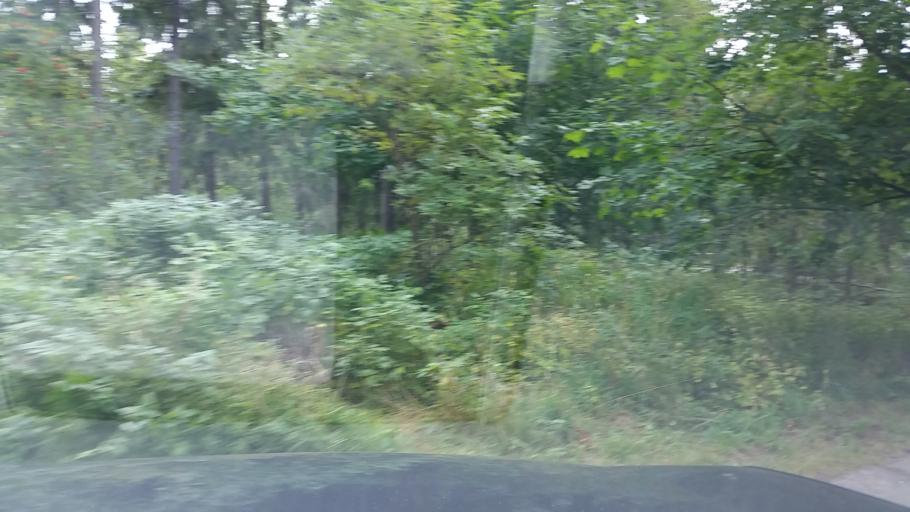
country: FI
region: Uusimaa
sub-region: Helsinki
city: Teekkarikylae
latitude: 60.1578
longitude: 24.8679
